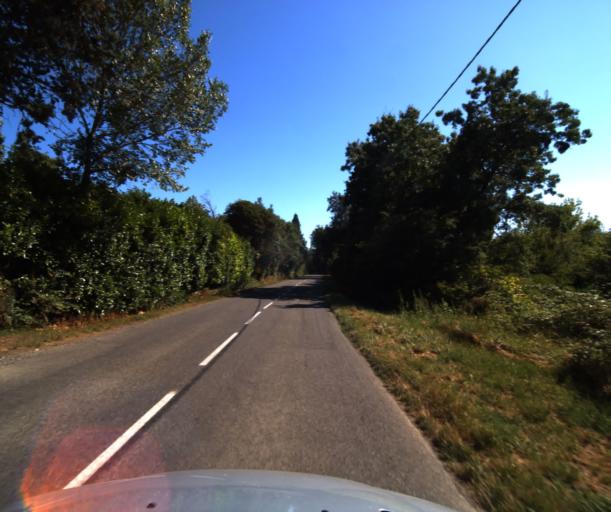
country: FR
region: Midi-Pyrenees
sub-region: Departement de la Haute-Garonne
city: Eaunes
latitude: 43.4396
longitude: 1.3277
